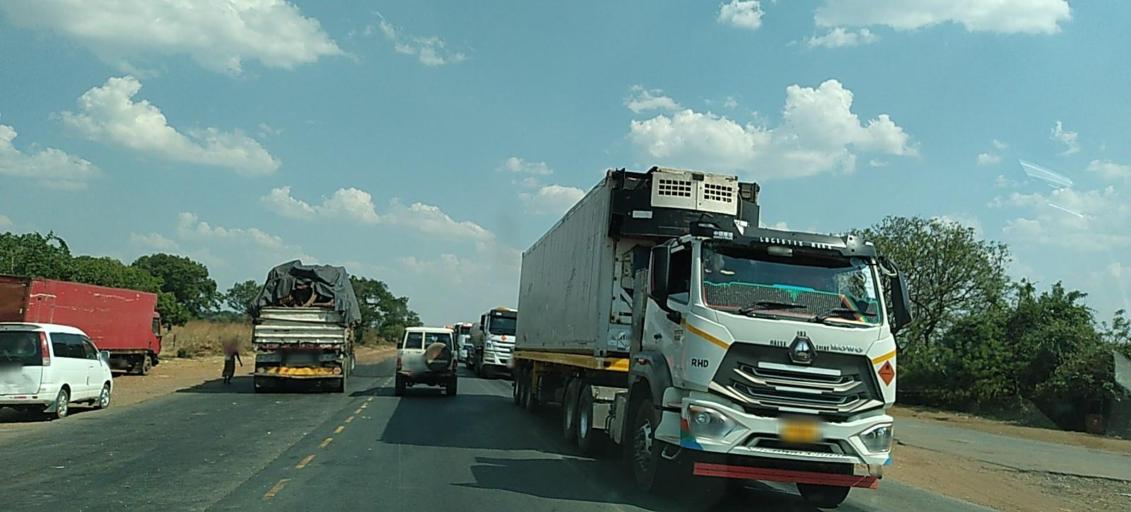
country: ZM
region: Central
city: Chibombo
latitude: -14.8811
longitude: 28.0614
